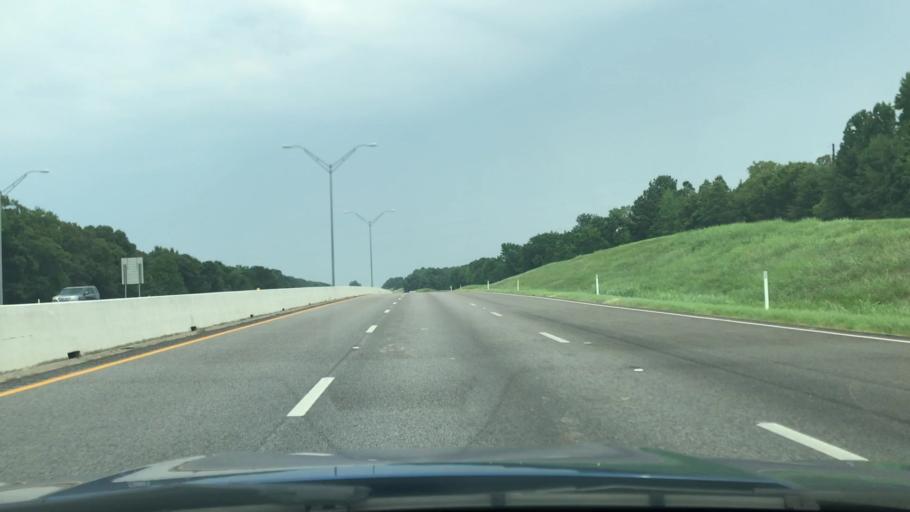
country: US
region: Texas
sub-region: Smith County
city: Tyler
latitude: 32.4519
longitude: -95.2268
